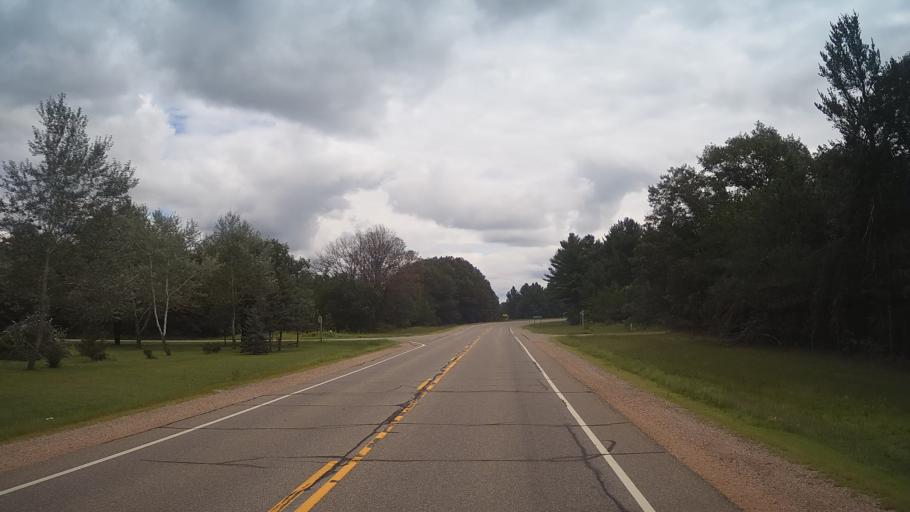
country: US
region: Wisconsin
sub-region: Adams County
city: Friendship
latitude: 44.0467
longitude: -89.9769
